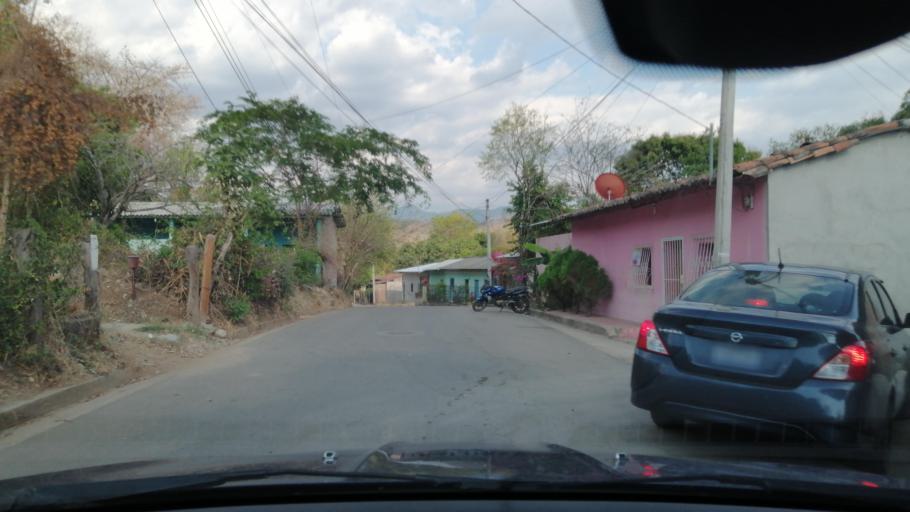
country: SV
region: Santa Ana
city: Metapan
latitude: 14.3292
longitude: -89.4294
